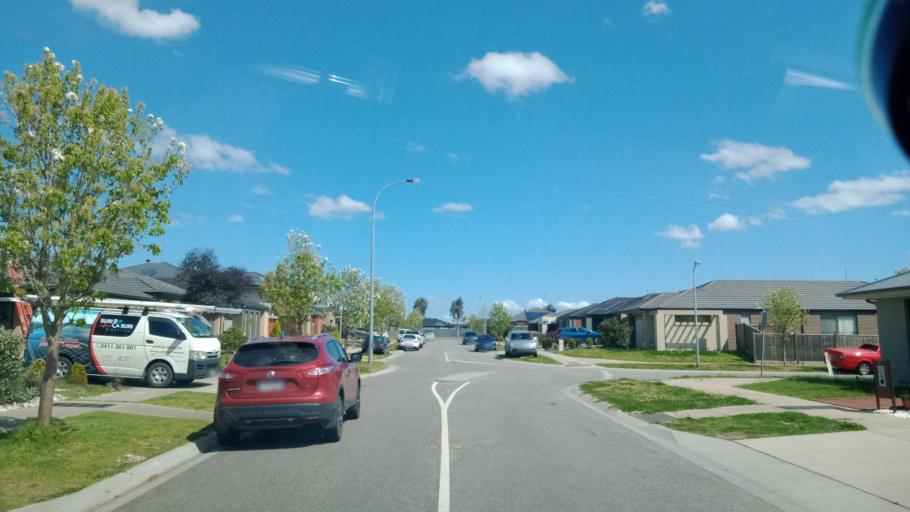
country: AU
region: Victoria
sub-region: Casey
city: Cranbourne West
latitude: -38.1005
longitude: 145.2529
